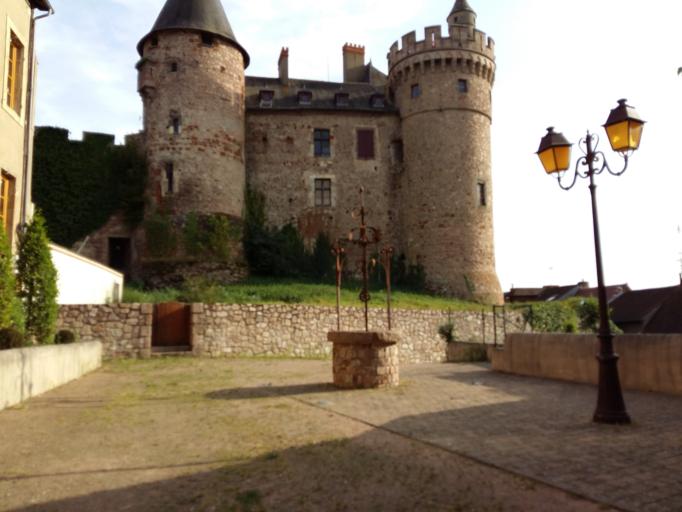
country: FR
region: Auvergne
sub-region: Departement de l'Allier
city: Lapalisse
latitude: 46.2492
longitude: 3.6381
